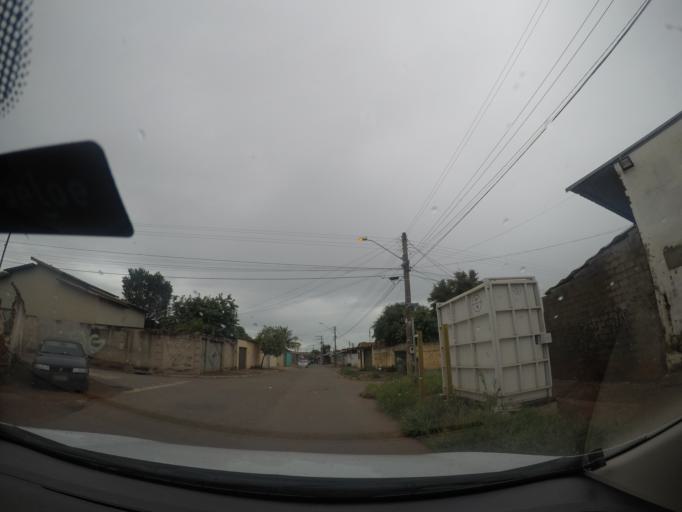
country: BR
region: Goias
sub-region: Goiania
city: Goiania
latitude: -16.6493
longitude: -49.3197
